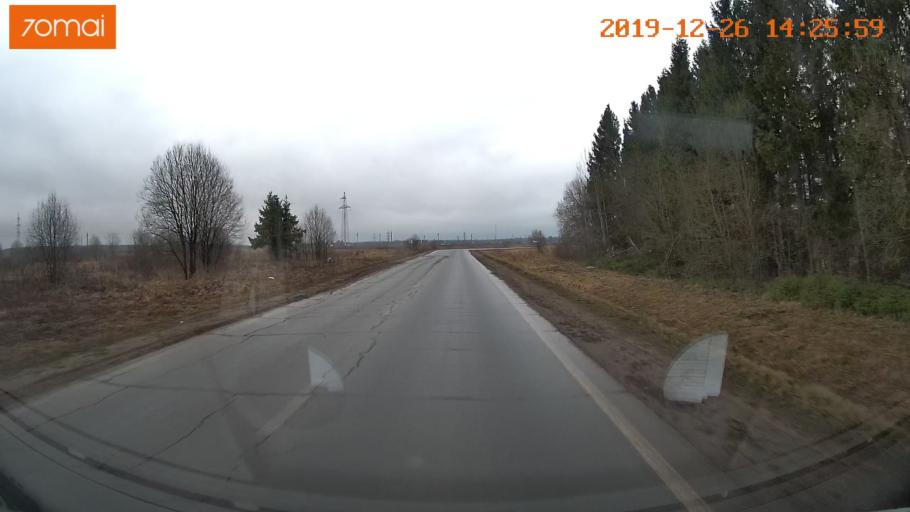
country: RU
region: Jaroslavl
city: Poshekhon'ye
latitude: 58.4897
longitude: 39.0911
